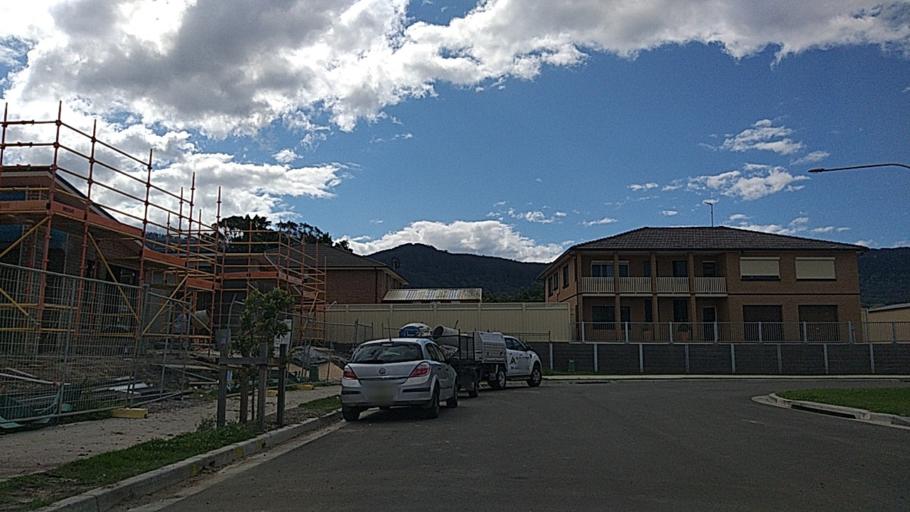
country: AU
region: New South Wales
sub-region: Wollongong
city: Dapto
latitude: -34.4809
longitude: 150.7667
